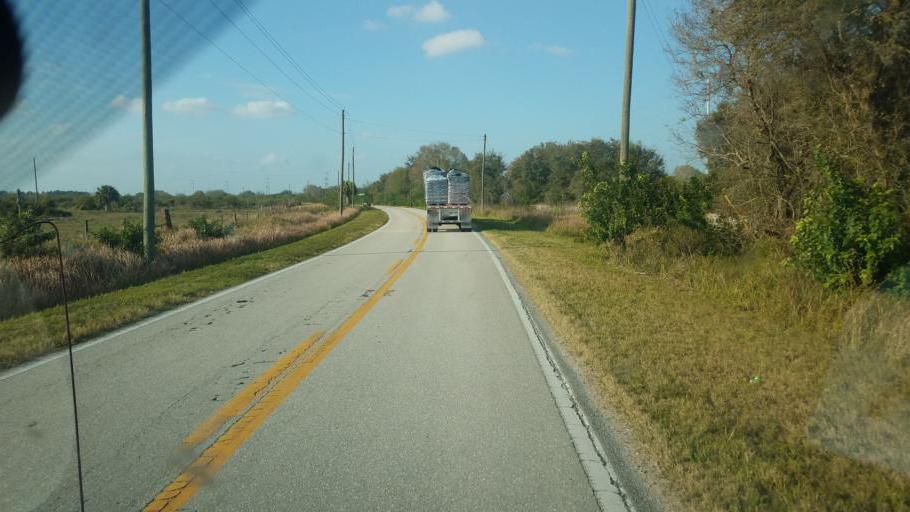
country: US
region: Florida
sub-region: Hardee County
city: Bowling Green
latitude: 27.7193
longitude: -81.9618
